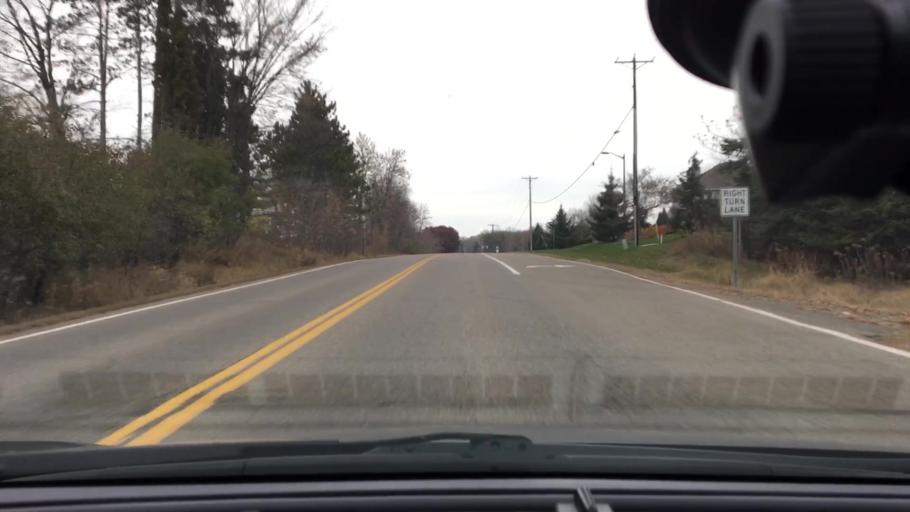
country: US
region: Minnesota
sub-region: Hennepin County
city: Corcoran
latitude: 45.0989
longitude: -93.5123
